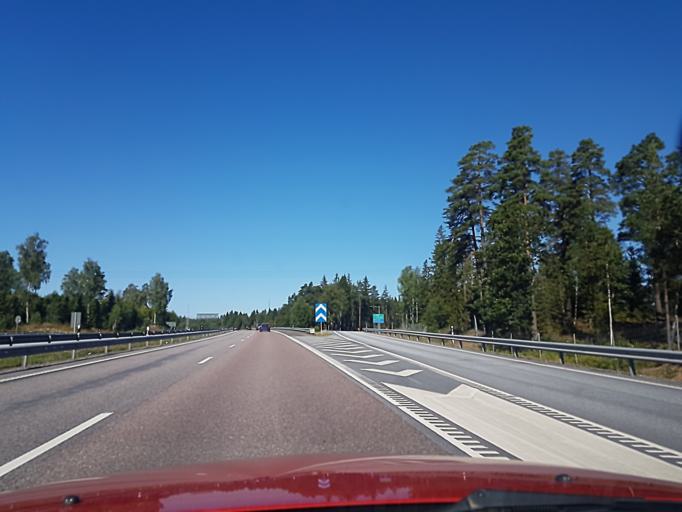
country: SE
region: Stockholm
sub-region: Nykvarns Kommun
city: Nykvarn
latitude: 59.1860
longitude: 17.5251
